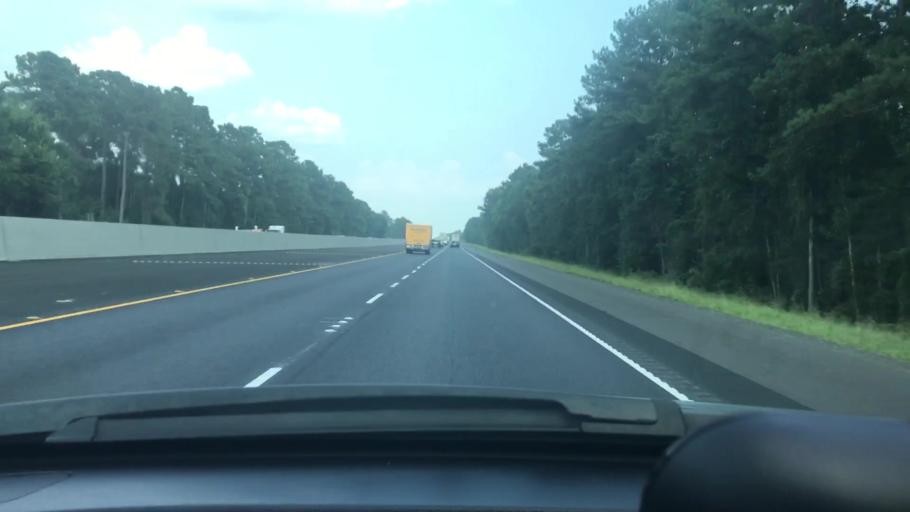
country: US
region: Louisiana
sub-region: Livingston Parish
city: Livingston
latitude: 30.4749
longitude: -90.6813
